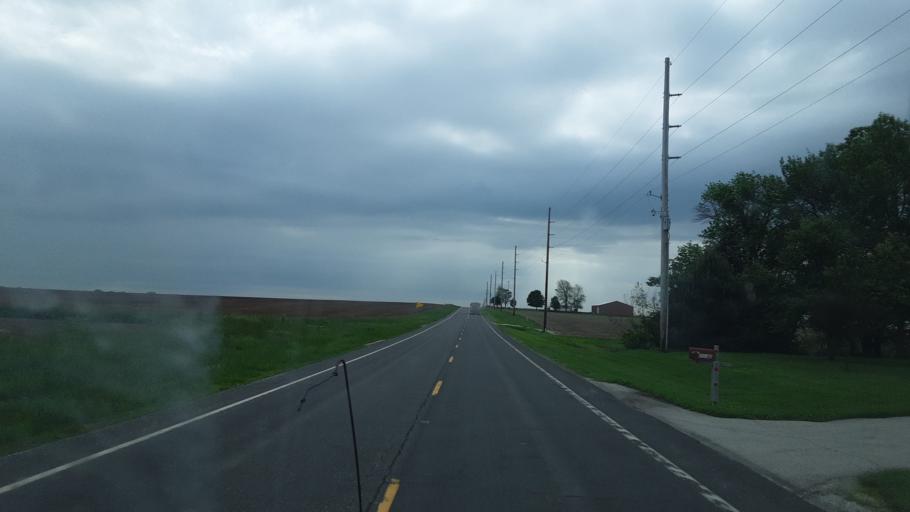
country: US
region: Illinois
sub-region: Fulton County
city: Astoria
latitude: 40.3568
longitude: -90.4110
